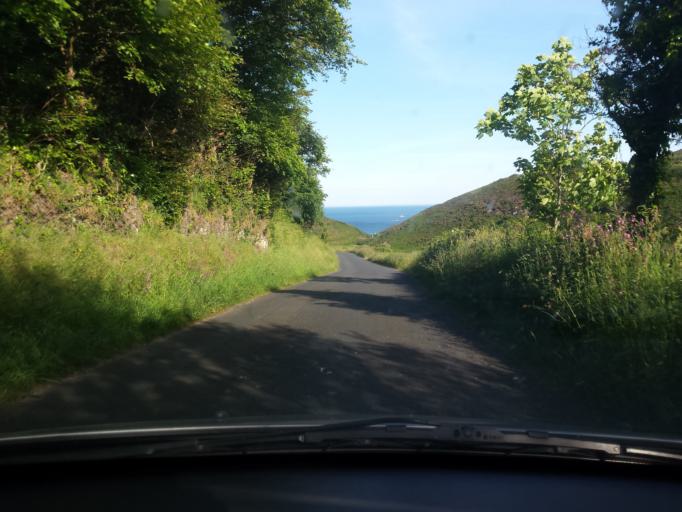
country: FR
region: Lower Normandy
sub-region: Departement de la Manche
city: Beaumont-Hague
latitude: 49.6876
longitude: -1.9278
